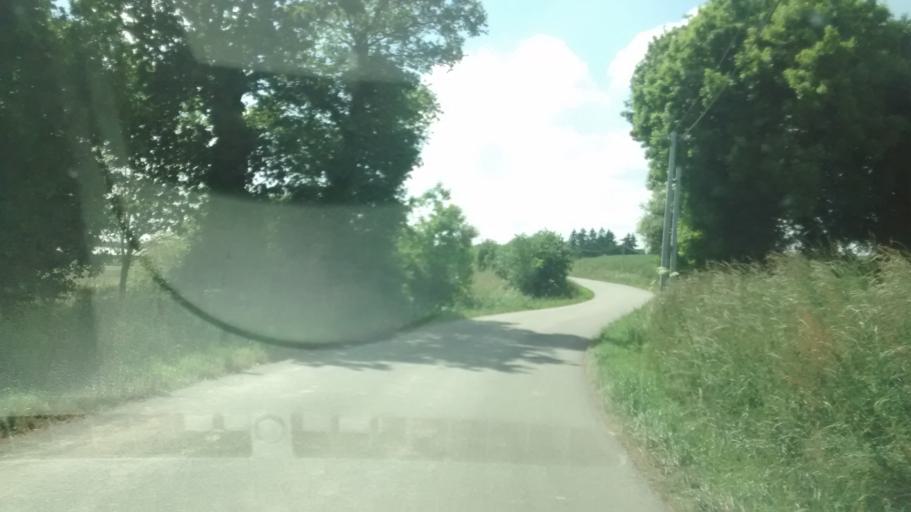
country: FR
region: Brittany
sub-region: Departement du Morbihan
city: Caro
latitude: 47.8753
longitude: -2.2945
